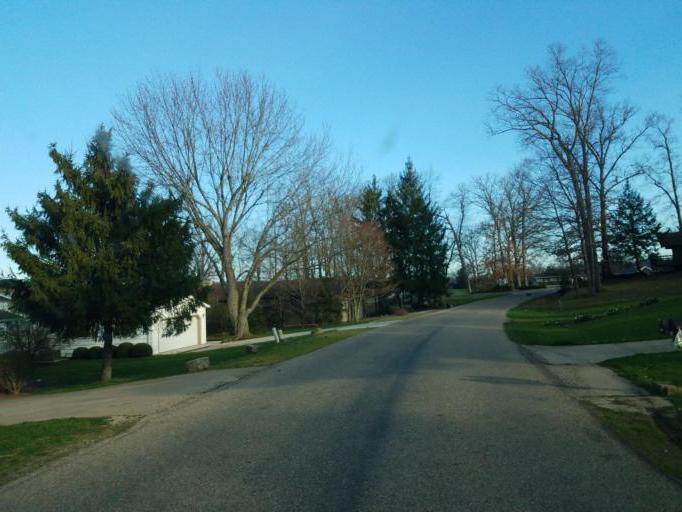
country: US
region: Ohio
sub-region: Knox County
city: Gambier
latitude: 40.4162
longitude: -82.3516
